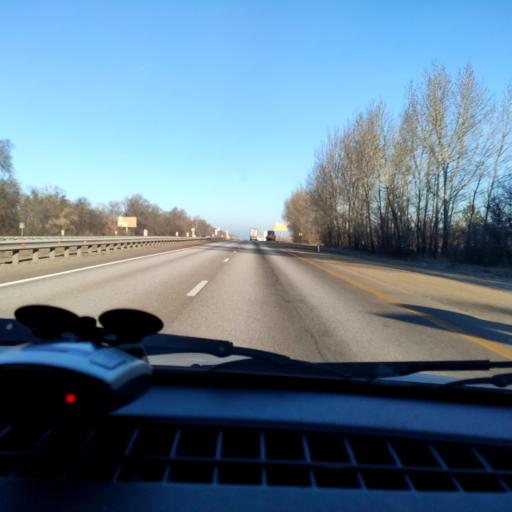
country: RU
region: Voronezj
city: Ramon'
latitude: 51.8995
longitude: 39.2188
